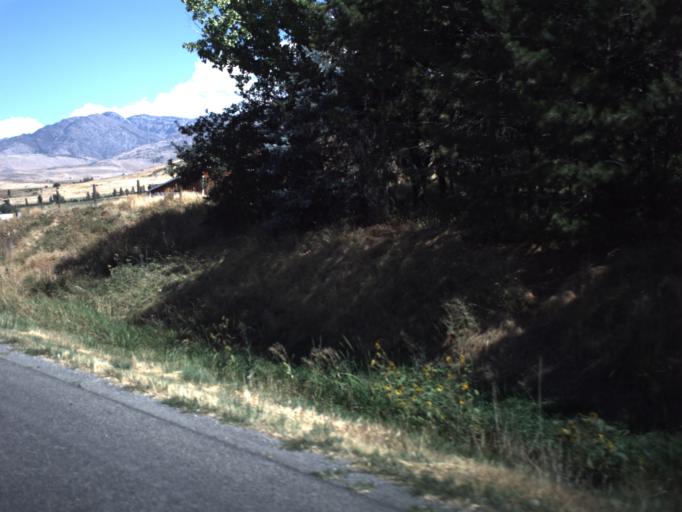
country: US
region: Utah
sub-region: Cache County
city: Smithfield
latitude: 41.8717
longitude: -111.8268
